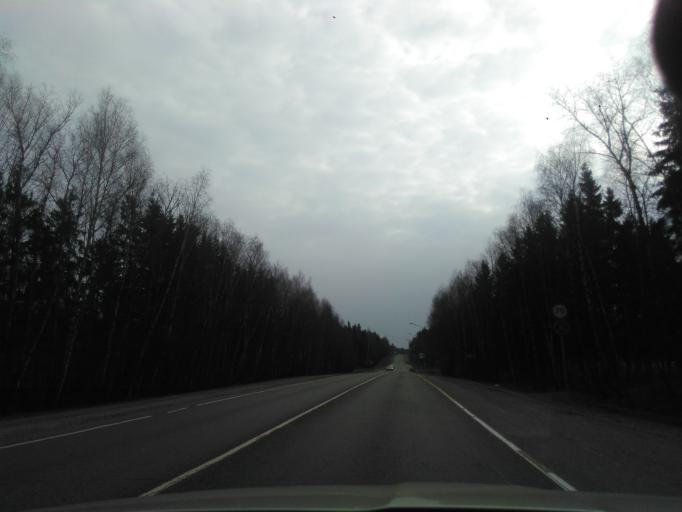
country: RU
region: Moskovskaya
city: Yermolino
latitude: 56.1368
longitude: 37.4513
